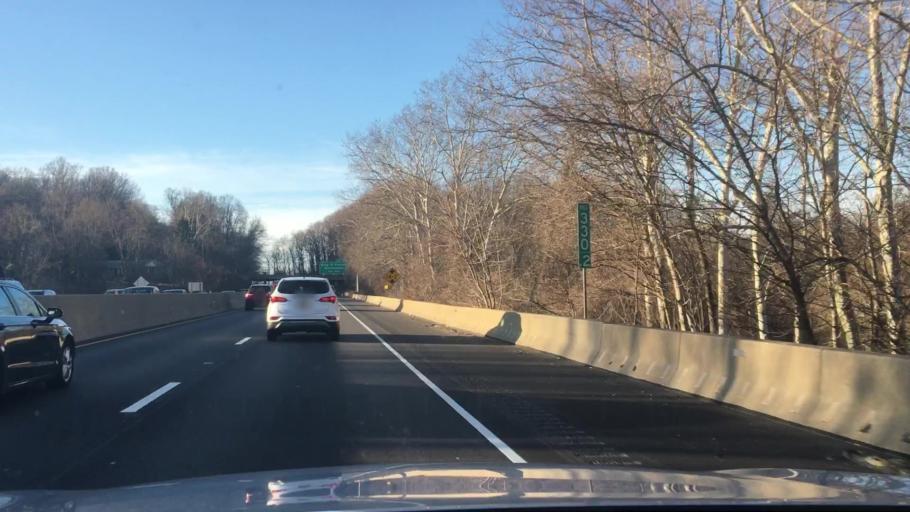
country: US
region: Pennsylvania
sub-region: Montgomery County
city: West Conshohocken
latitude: 40.0700
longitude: -75.3433
